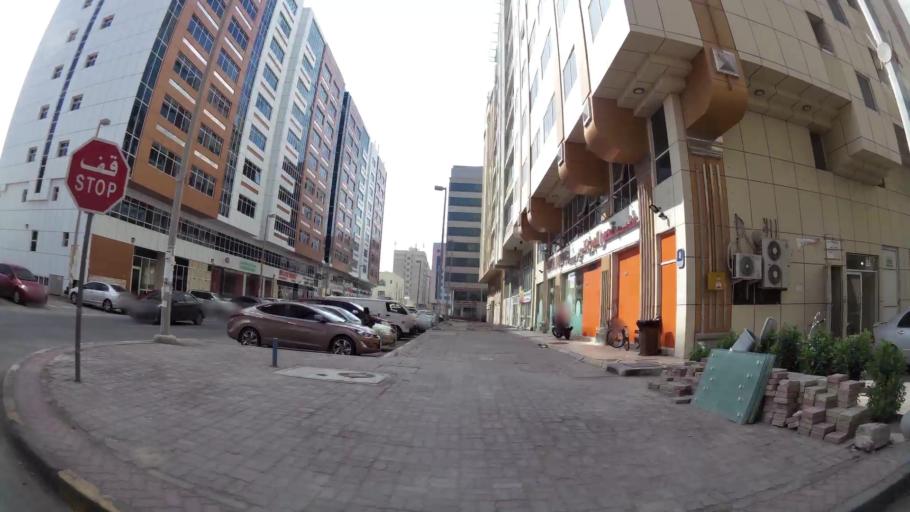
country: AE
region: Abu Dhabi
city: Abu Dhabi
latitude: 24.3364
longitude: 54.5341
